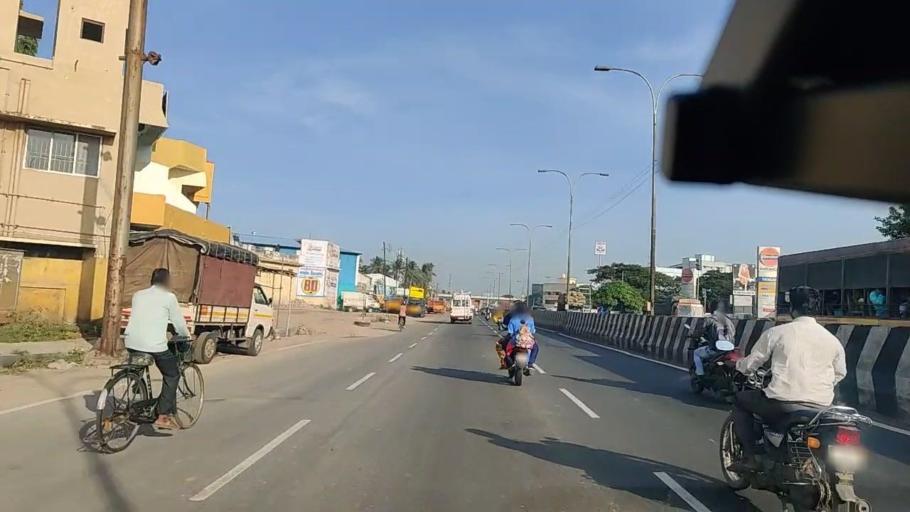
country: IN
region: Tamil Nadu
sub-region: Thiruvallur
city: Chinnasekkadu
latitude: 13.1424
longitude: 80.2232
